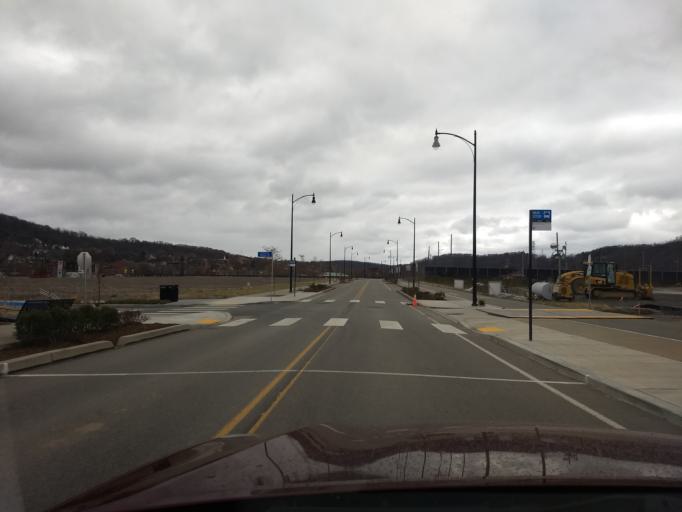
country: US
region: Pennsylvania
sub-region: Allegheny County
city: Mount Oliver
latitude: 40.4134
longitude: -79.9497
